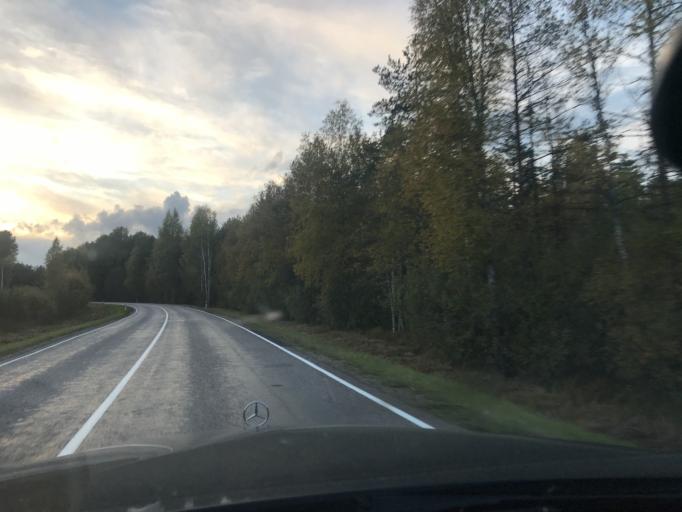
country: EE
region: Valgamaa
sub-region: Torva linn
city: Torva
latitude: 58.0100
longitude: 26.1385
